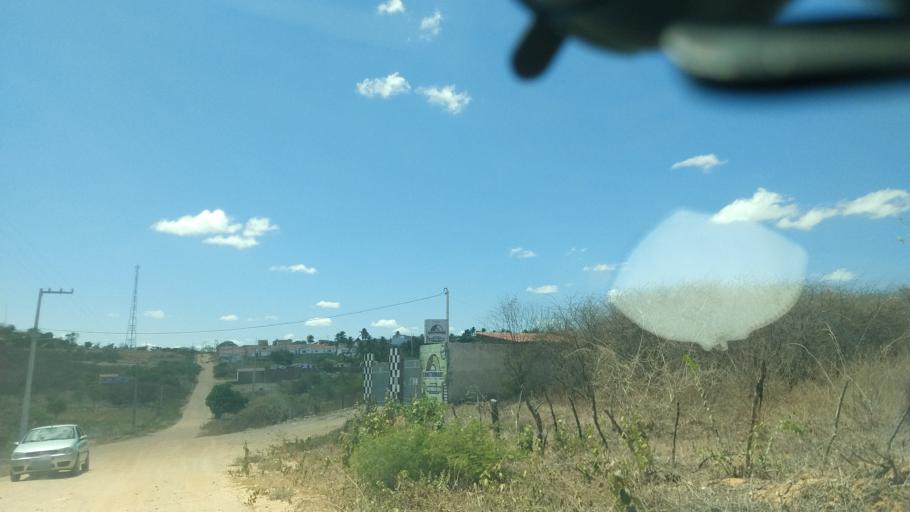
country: BR
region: Rio Grande do Norte
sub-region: Cerro Cora
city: Cerro Cora
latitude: -6.0310
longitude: -36.3416
